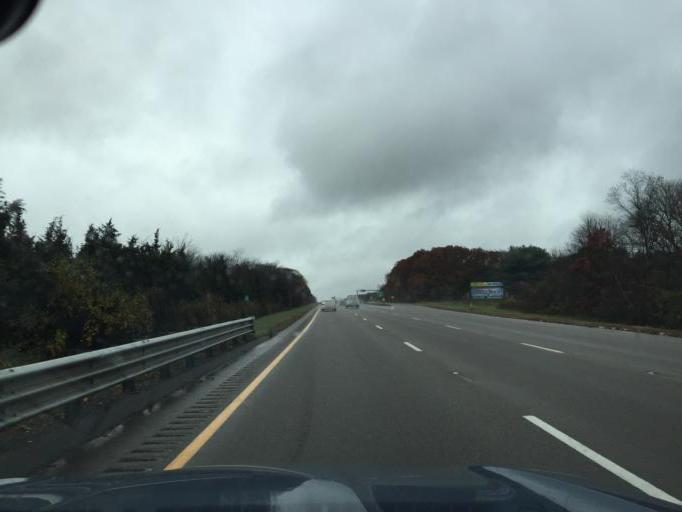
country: US
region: Massachusetts
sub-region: Bristol County
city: North Seekonk
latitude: 41.9134
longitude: -71.3355
